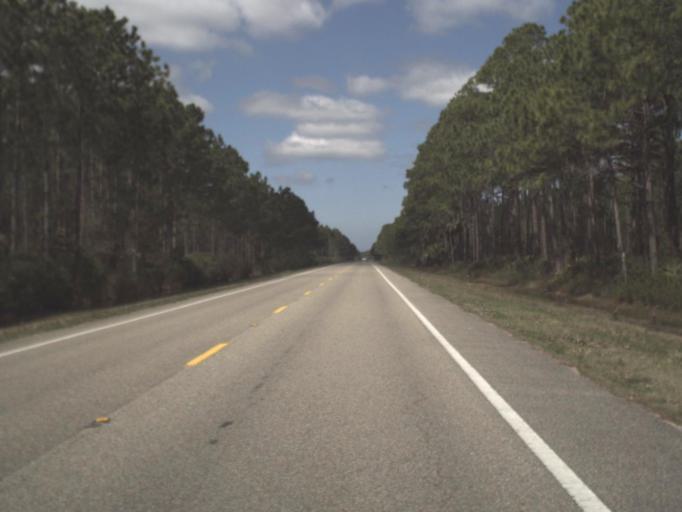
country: US
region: Florida
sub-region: Franklin County
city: Apalachicola
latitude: 29.7253
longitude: -85.1236
